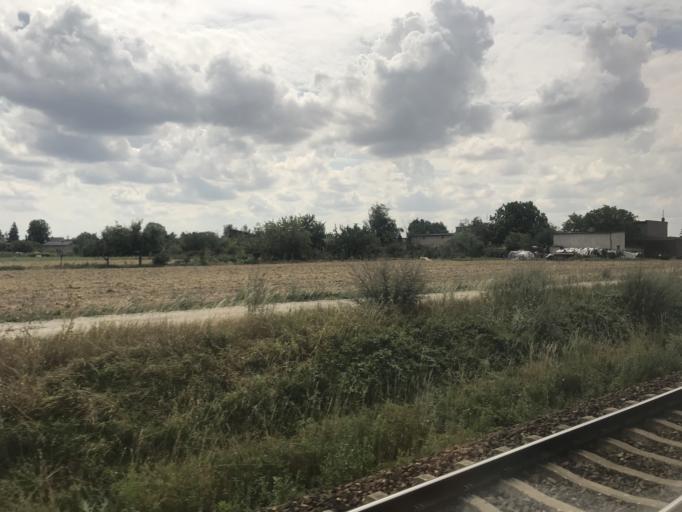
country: PL
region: Greater Poland Voivodeship
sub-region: Powiat poznanski
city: Dopiewo
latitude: 52.3638
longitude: 16.7063
